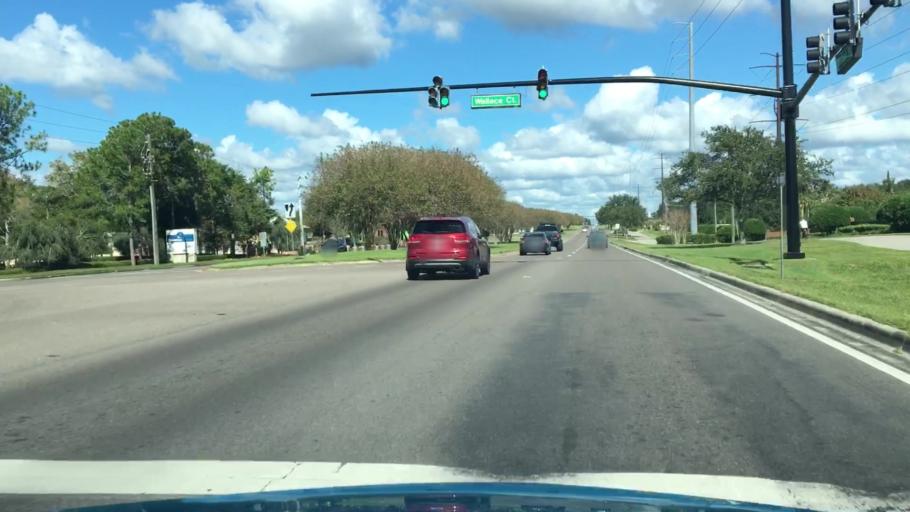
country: US
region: Florida
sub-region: Seminole County
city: Heathrow
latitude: 28.7742
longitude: -81.3470
